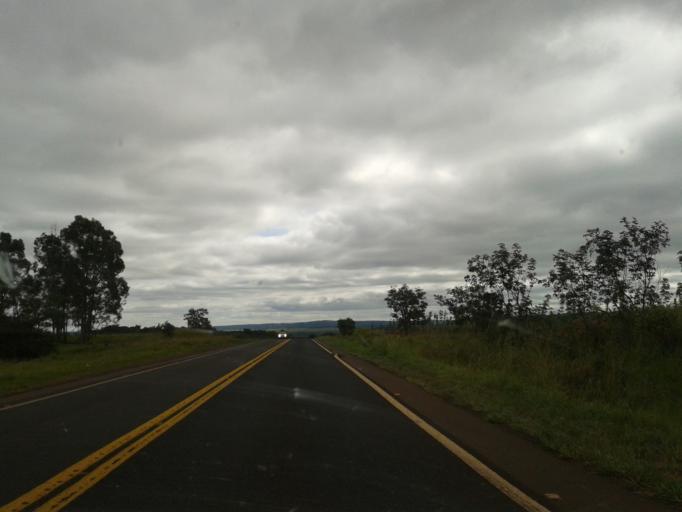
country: BR
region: Minas Gerais
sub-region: Campina Verde
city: Campina Verde
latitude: -19.5222
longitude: -49.6302
